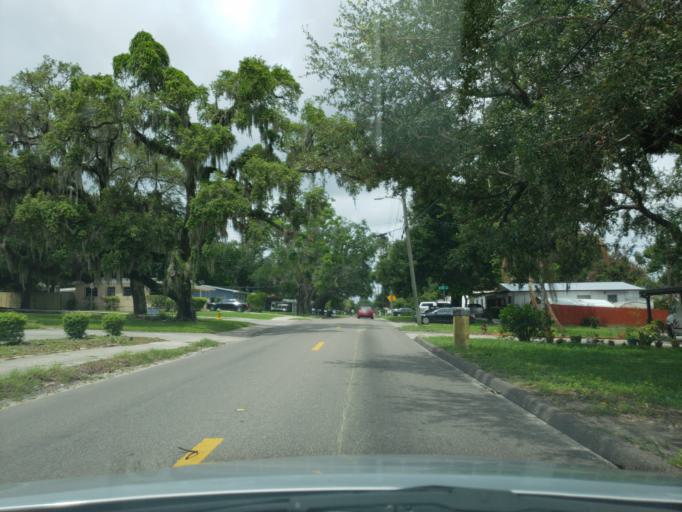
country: US
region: Florida
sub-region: Hillsborough County
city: Temple Terrace
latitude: 28.0034
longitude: -82.4199
